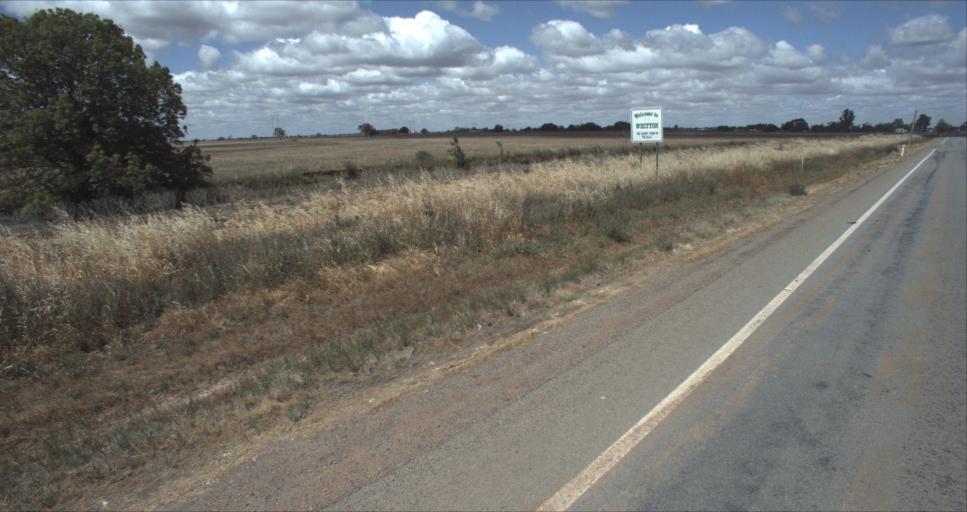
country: AU
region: New South Wales
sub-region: Murrumbidgee Shire
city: Darlington Point
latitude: -34.5115
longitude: 146.1862
